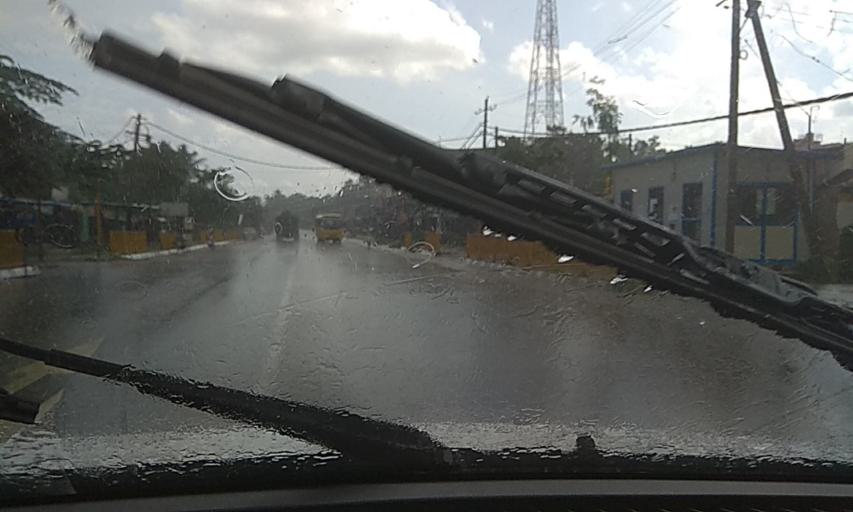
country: IN
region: Karnataka
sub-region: Mandya
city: Maddur
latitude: 12.6913
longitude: 77.0599
